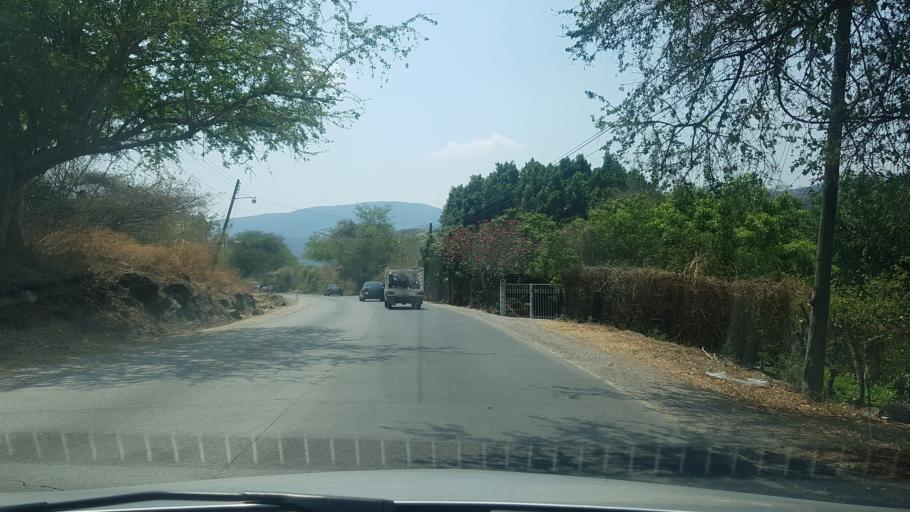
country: MX
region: Morelos
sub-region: Jiutepec
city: Independencia
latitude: 18.8037
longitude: -99.0929
